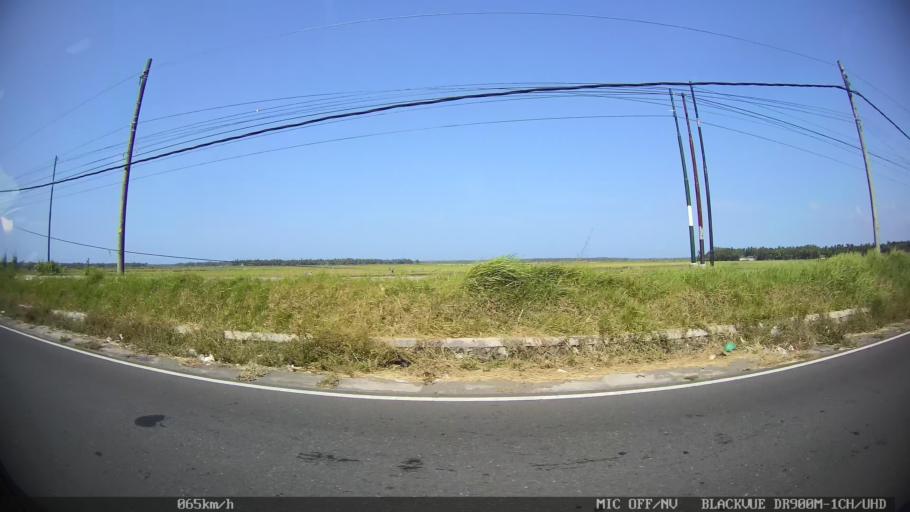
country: ID
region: Daerah Istimewa Yogyakarta
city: Srandakan
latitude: -7.9278
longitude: 110.1902
